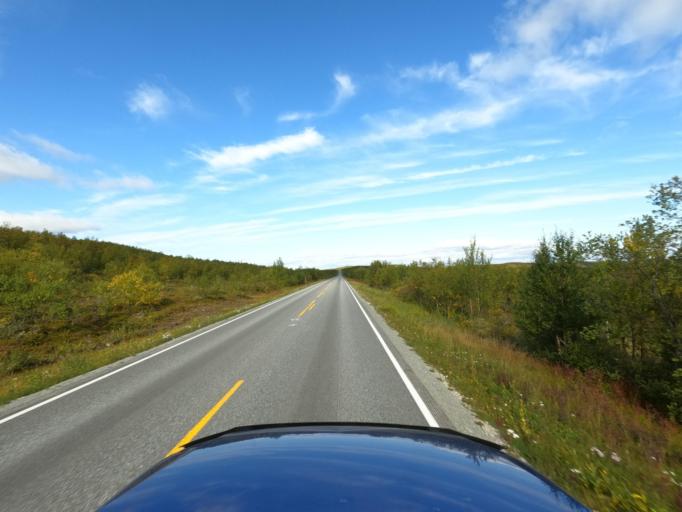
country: NO
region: Finnmark Fylke
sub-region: Karasjok
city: Karasjohka
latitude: 69.6863
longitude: 25.2609
